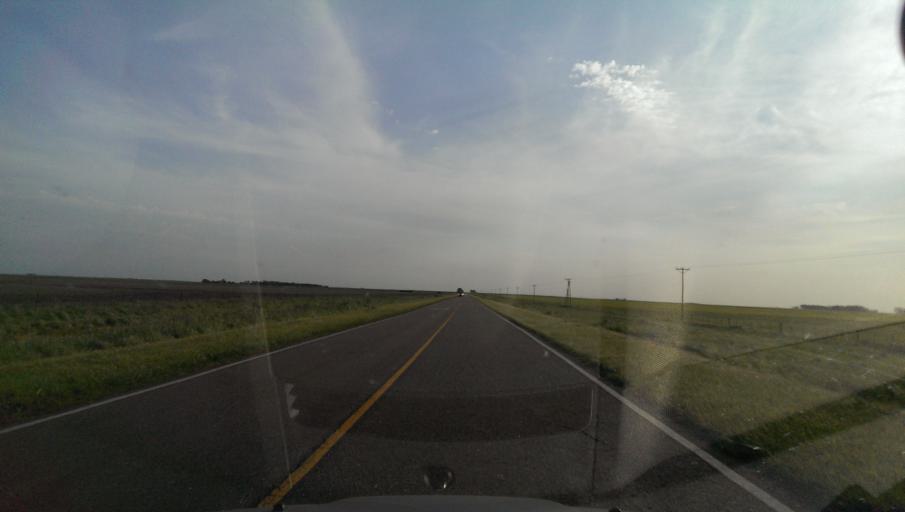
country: AR
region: Buenos Aires
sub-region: Partido de General La Madrid
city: General La Madrid
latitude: -37.5780
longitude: -61.3525
